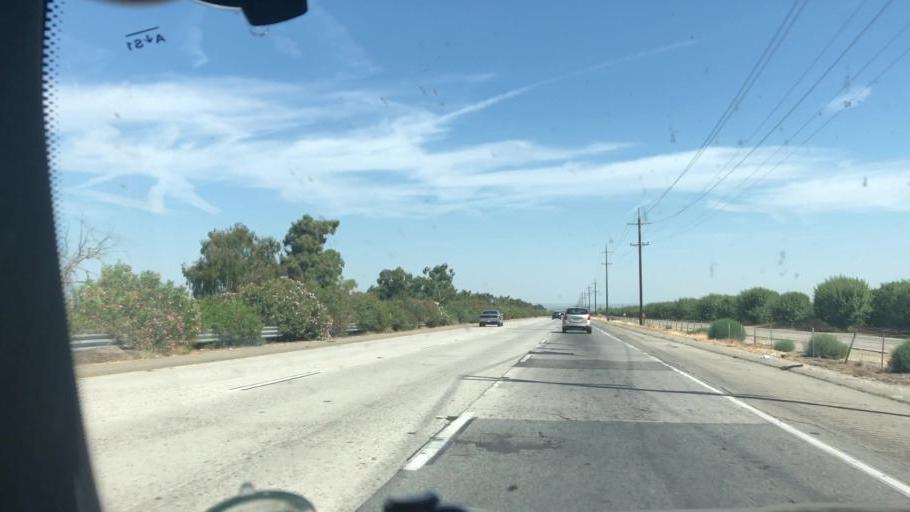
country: US
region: California
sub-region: Kern County
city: Weedpatch
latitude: 35.0374
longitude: -118.9613
